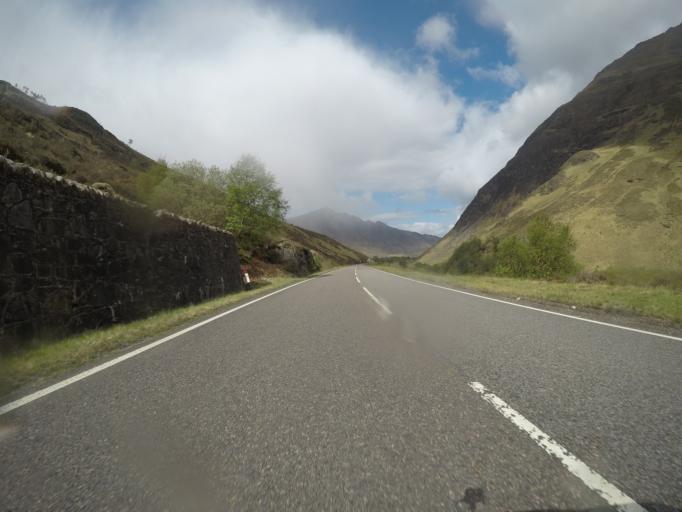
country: GB
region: Scotland
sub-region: Highland
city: Fort William
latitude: 57.1654
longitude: -5.3399
